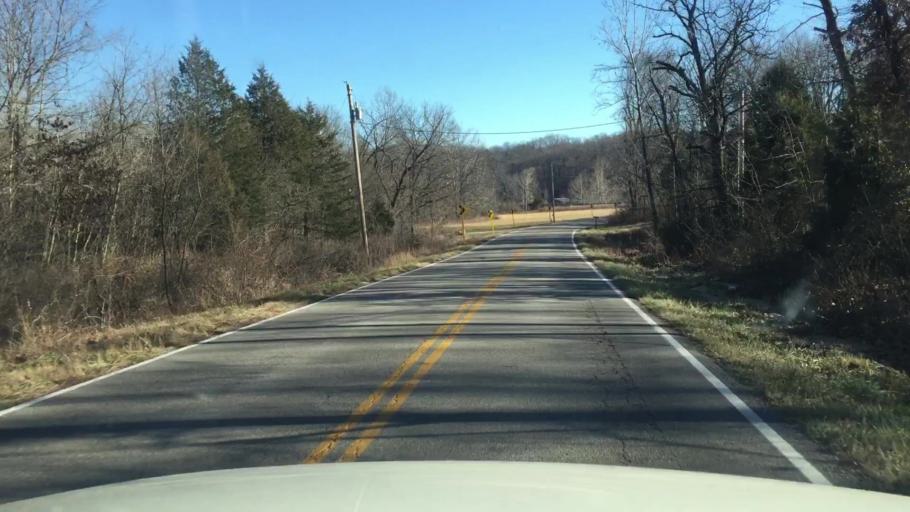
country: US
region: Missouri
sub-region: Miller County
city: Eldon
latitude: 38.3400
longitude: -92.7221
